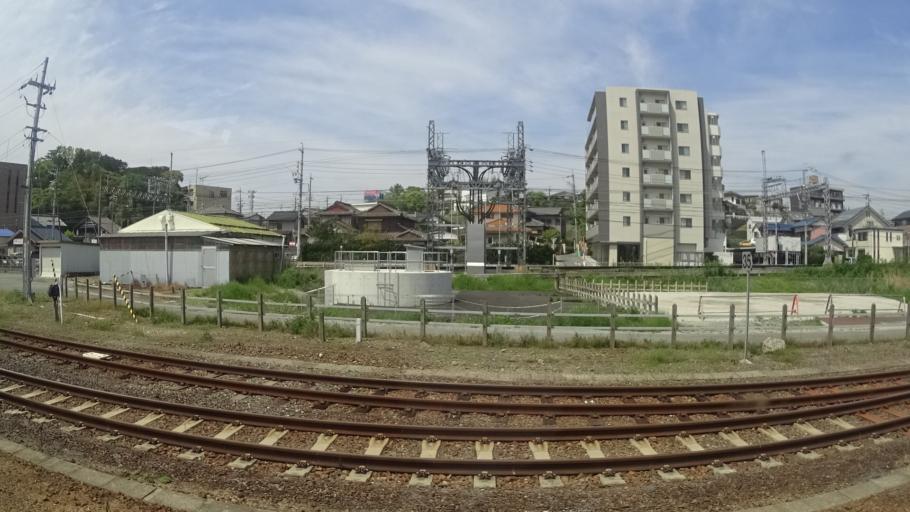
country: JP
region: Mie
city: Tsu-shi
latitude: 34.7359
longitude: 136.5106
